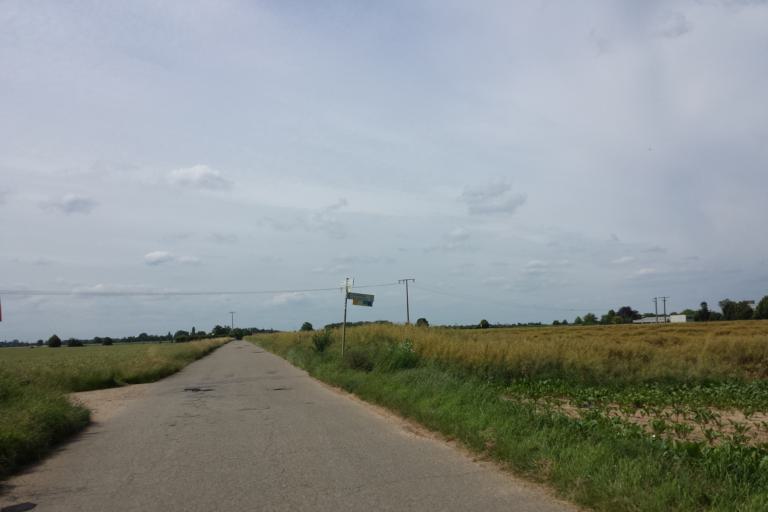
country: DE
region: Baden-Wuerttemberg
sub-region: Karlsruhe Region
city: Dossenheim
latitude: 49.4451
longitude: 8.6403
